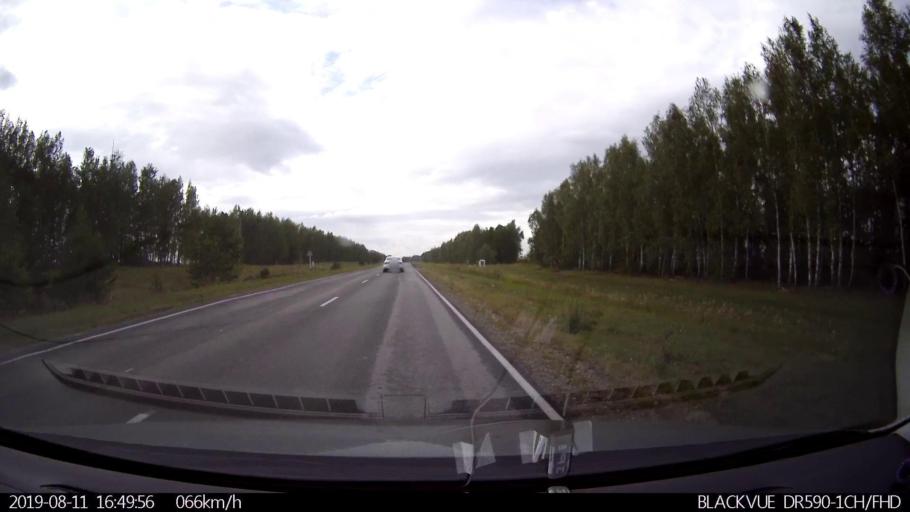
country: RU
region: Ulyanovsk
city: Mayna
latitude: 54.2246
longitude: 47.6930
